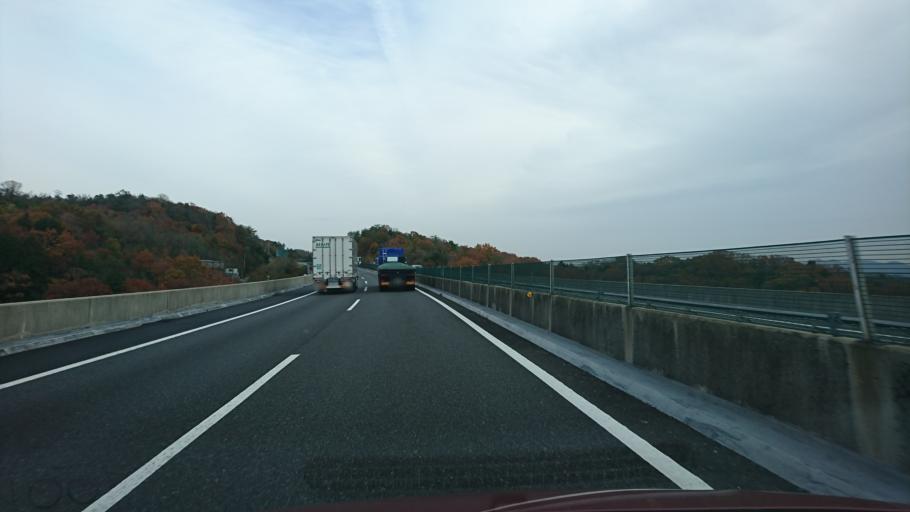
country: JP
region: Hyogo
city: Miki
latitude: 34.8175
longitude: 134.9912
